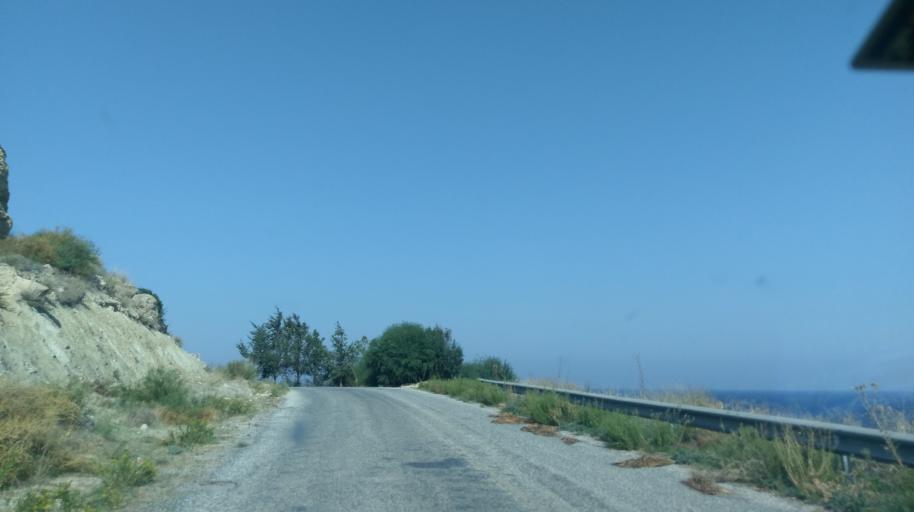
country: CY
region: Keryneia
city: Lapithos
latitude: 35.3570
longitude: 33.0469
